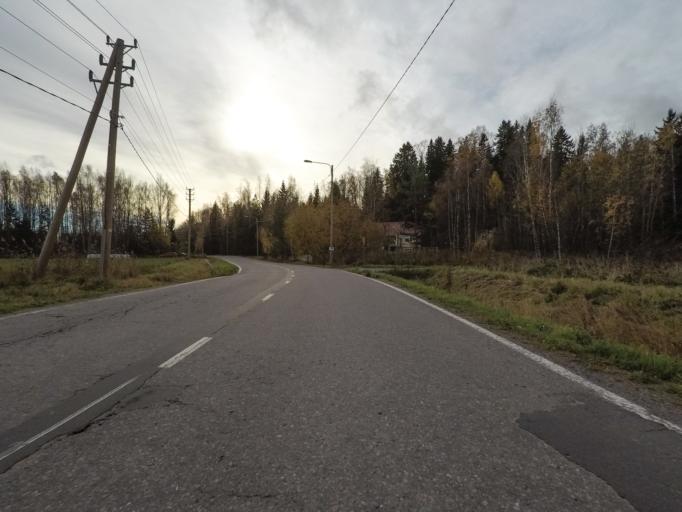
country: FI
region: Uusimaa
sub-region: Helsinki
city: Vantaa
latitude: 60.2682
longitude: 25.1385
